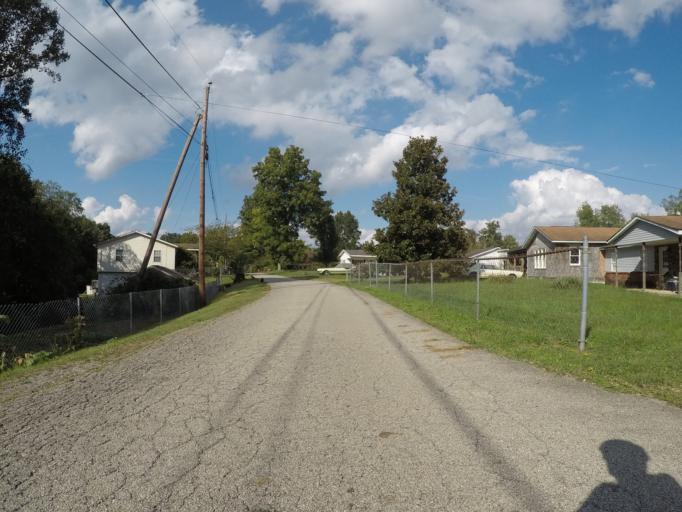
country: US
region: West Virginia
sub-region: Wayne County
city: Lavalette
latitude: 38.3628
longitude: -82.4557
